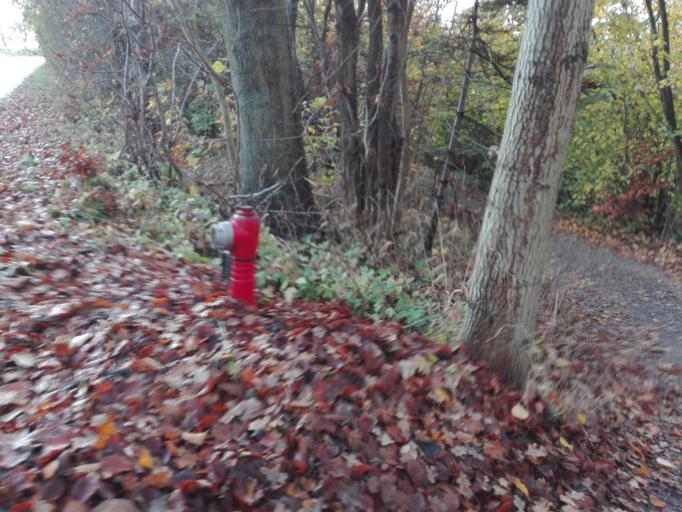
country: DK
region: Central Jutland
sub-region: Arhus Kommune
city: Beder
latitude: 56.0798
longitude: 10.2340
